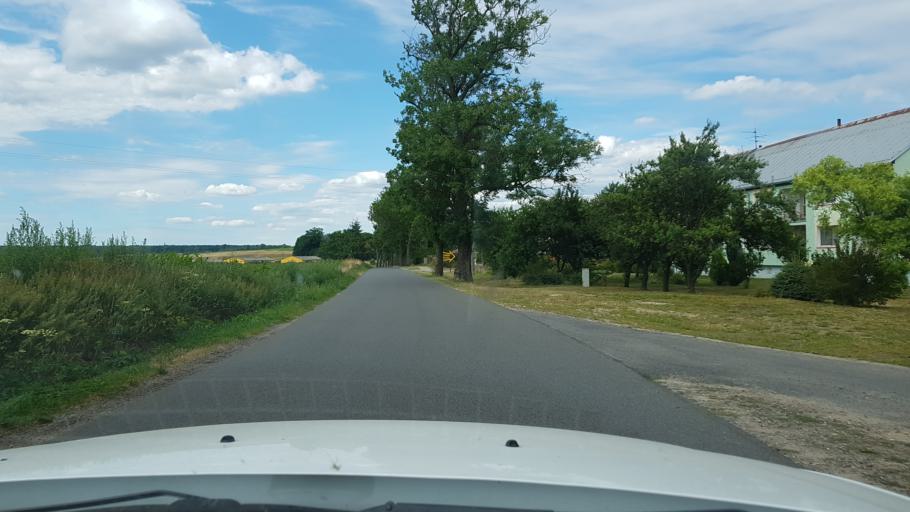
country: PL
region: West Pomeranian Voivodeship
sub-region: Powiat drawski
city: Kalisz Pomorski
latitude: 53.3327
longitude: 15.9312
